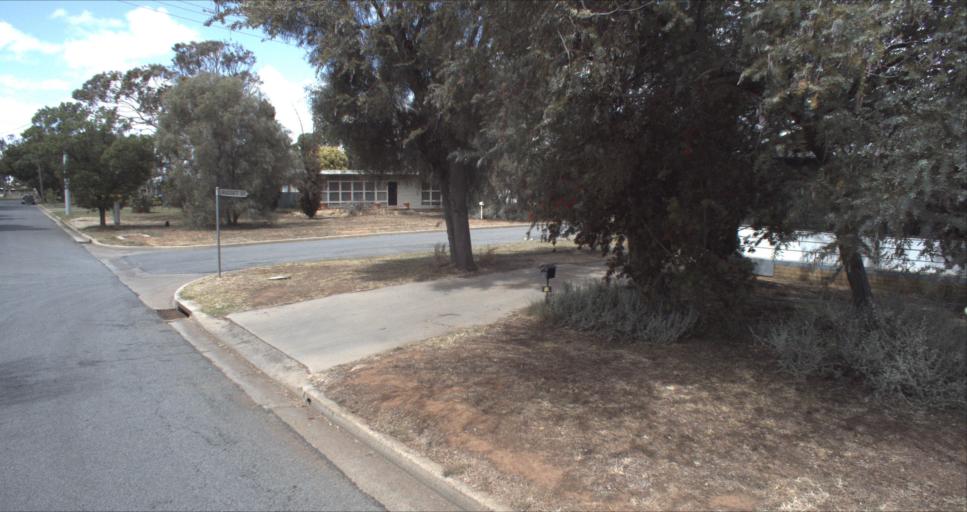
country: AU
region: New South Wales
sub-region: Leeton
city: Leeton
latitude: -34.5544
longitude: 146.3893
